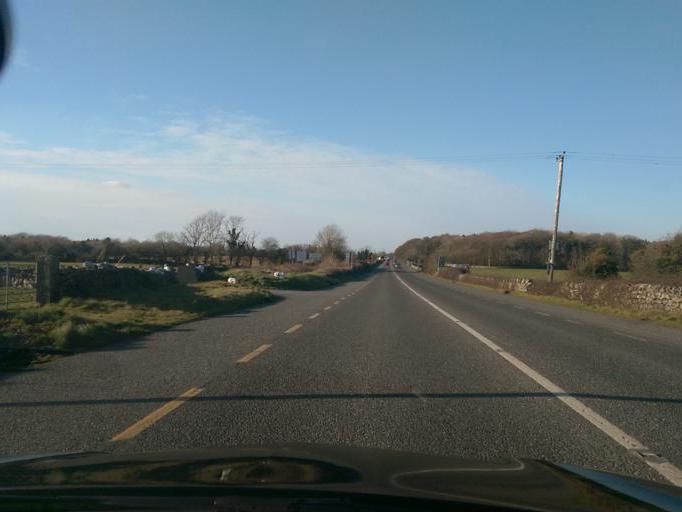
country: IE
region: Connaught
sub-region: County Galway
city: Oranmore
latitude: 53.2191
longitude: -8.8735
